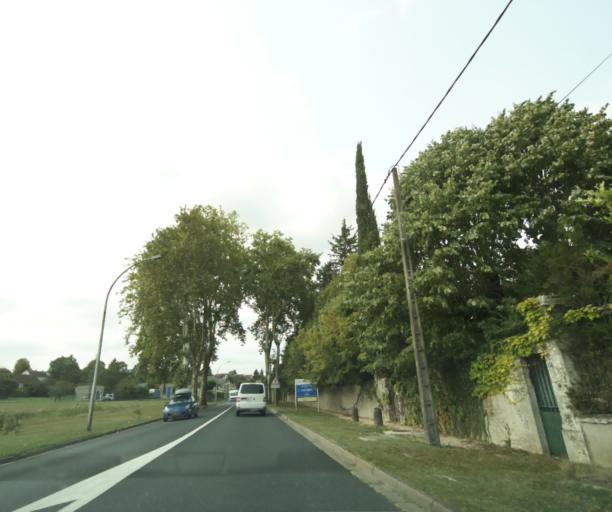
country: FR
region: Centre
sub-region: Departement de l'Indre
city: Chatillon-sur-Indre
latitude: 46.9790
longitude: 1.1789
